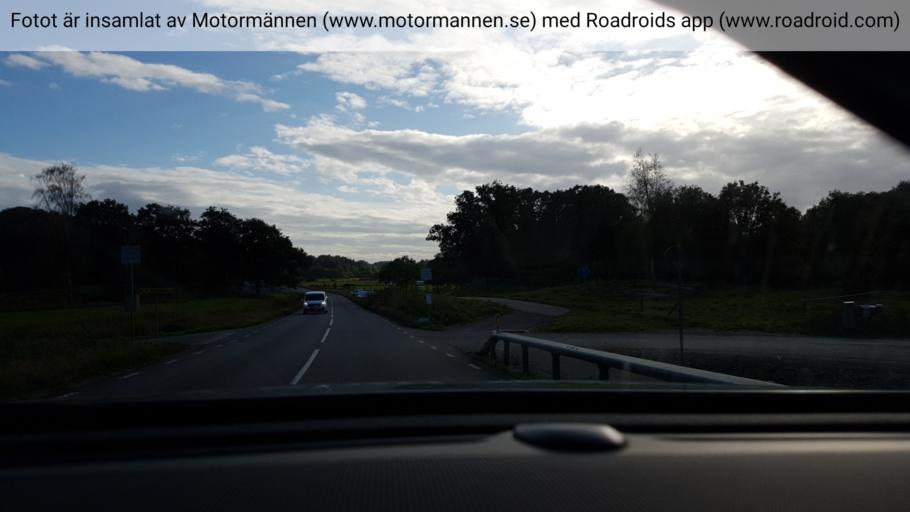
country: SE
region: Vaestra Goetaland
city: Svanesund
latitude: 58.1230
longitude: 11.8571
